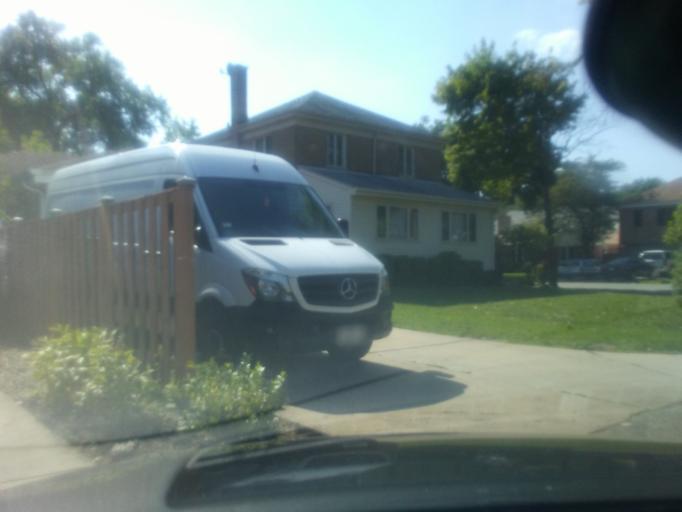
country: US
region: Illinois
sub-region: Cook County
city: Lincolnwood
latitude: 41.9848
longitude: -87.7465
